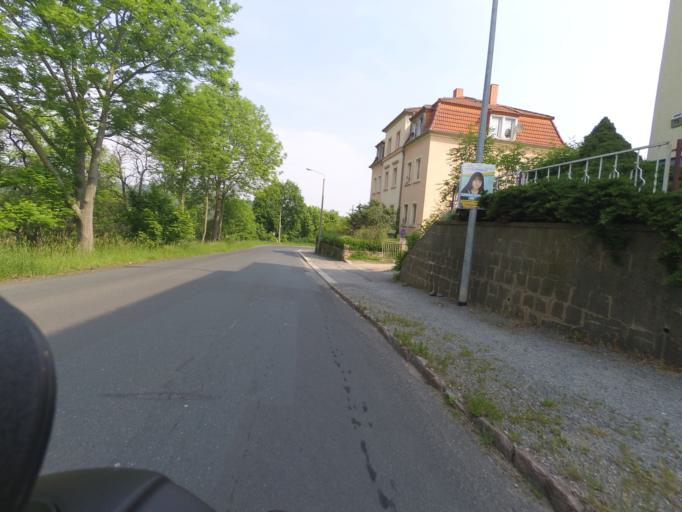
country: DE
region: Saxony
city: Rabenau
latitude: 50.9740
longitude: 13.6310
